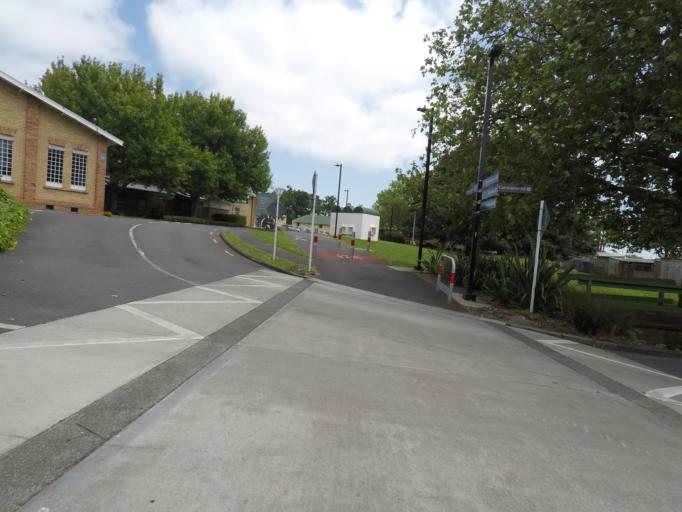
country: NZ
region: Auckland
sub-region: Auckland
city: Rosebank
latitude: -36.8820
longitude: 174.7048
